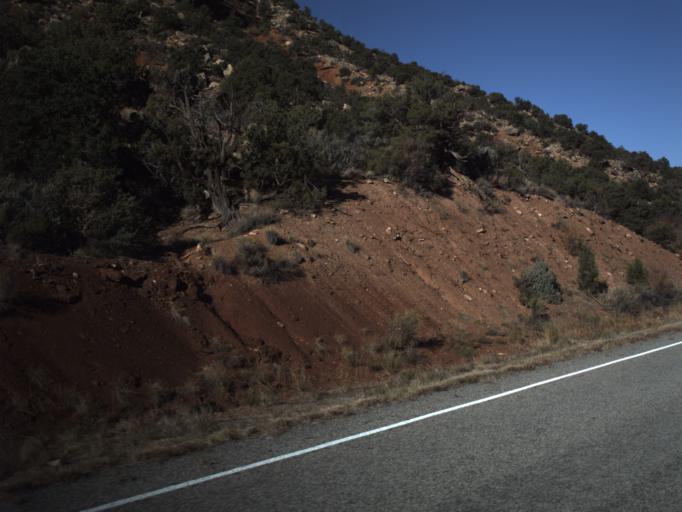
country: US
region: Utah
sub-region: San Juan County
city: Blanding
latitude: 37.5959
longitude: -110.0469
